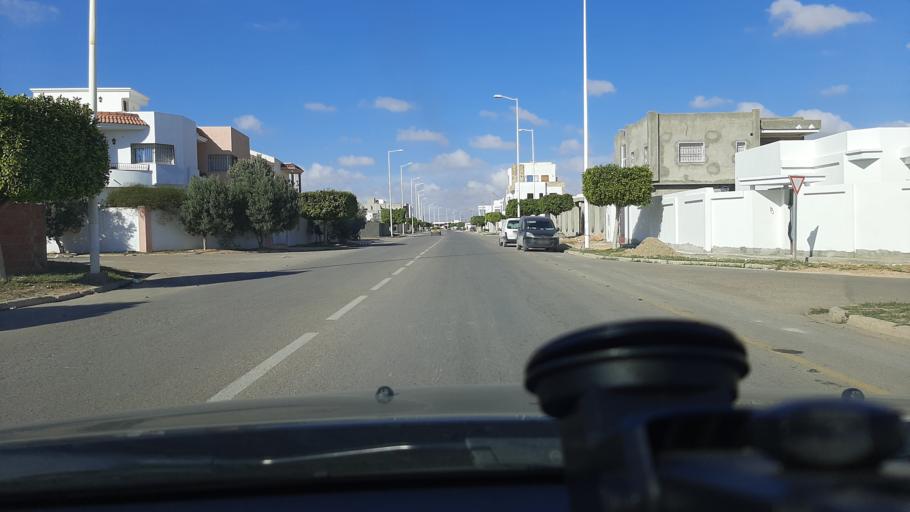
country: TN
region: Safaqis
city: Sfax
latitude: 34.8077
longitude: 10.7127
